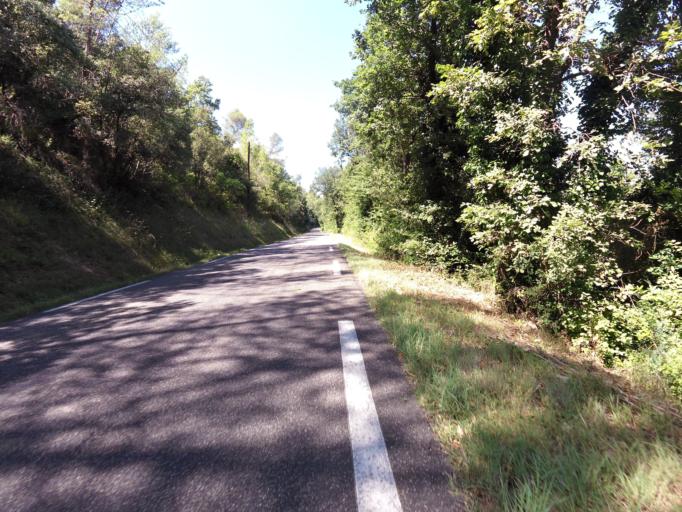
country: FR
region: Languedoc-Roussillon
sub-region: Departement du Gard
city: Sommieres
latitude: 43.8218
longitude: 4.0678
